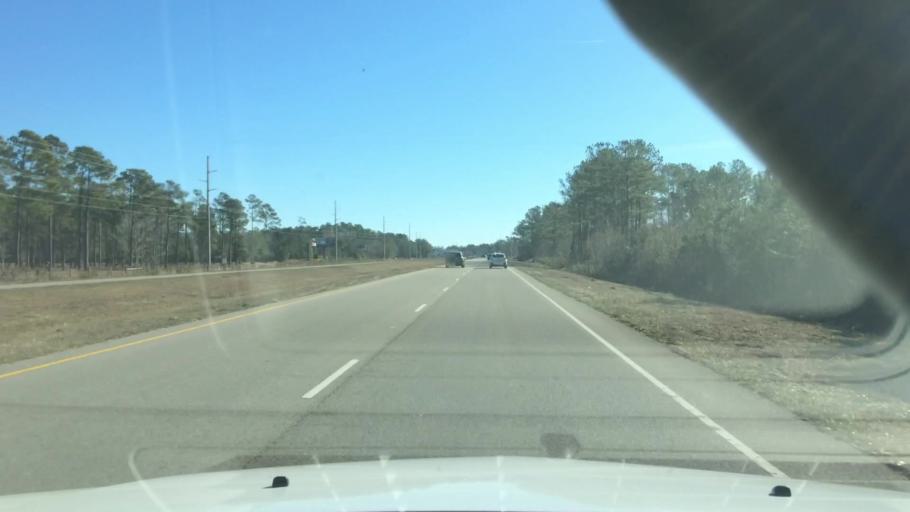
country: US
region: North Carolina
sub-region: Brunswick County
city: Shallotte
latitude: 33.9876
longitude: -78.3721
